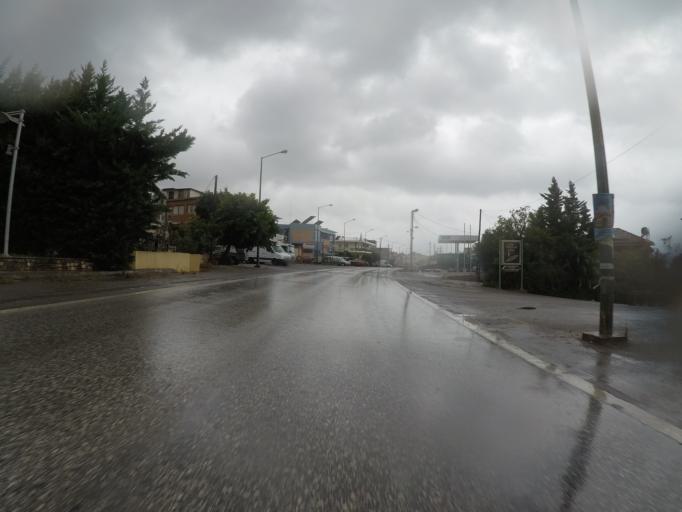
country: GR
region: Peloponnese
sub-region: Nomos Messinias
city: Kyparissia
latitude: 37.2526
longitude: 21.6757
